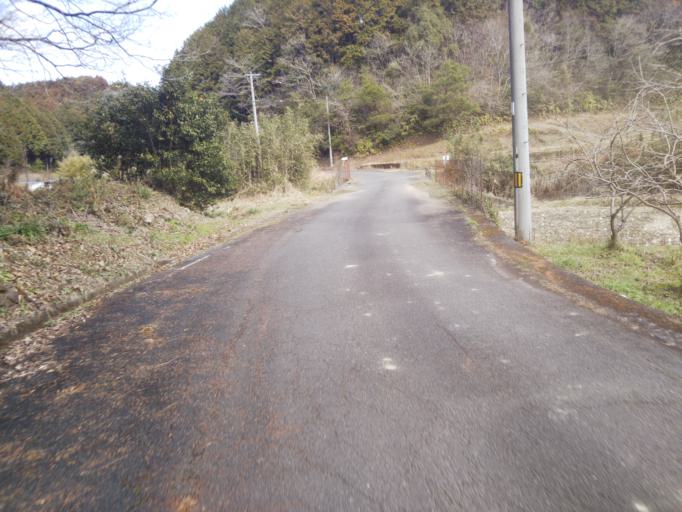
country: JP
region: Kochi
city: Nakamura
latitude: 33.0371
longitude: 132.9849
